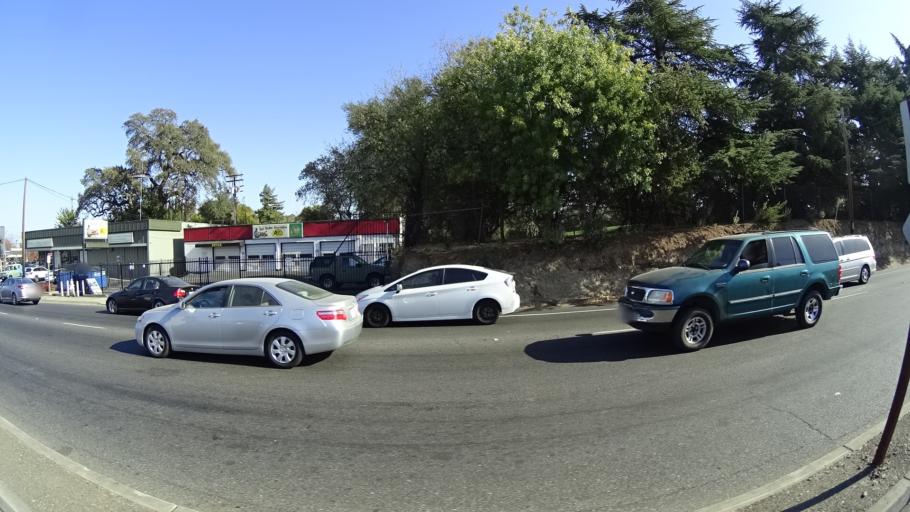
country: US
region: California
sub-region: Sacramento County
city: Fair Oaks
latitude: 38.6628
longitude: -121.2923
